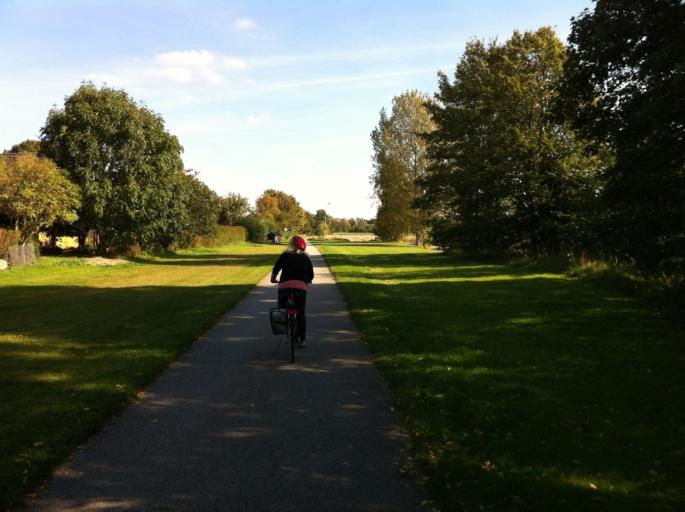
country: SE
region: Skane
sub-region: Lunds Kommun
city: Lund
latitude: 55.7891
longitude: 13.2052
